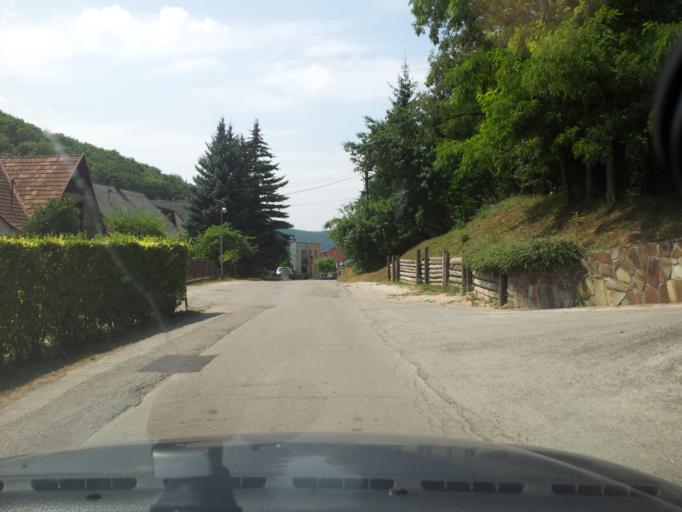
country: SK
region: Trenciansky
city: Nova Dubnica
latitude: 48.9089
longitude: 18.1059
